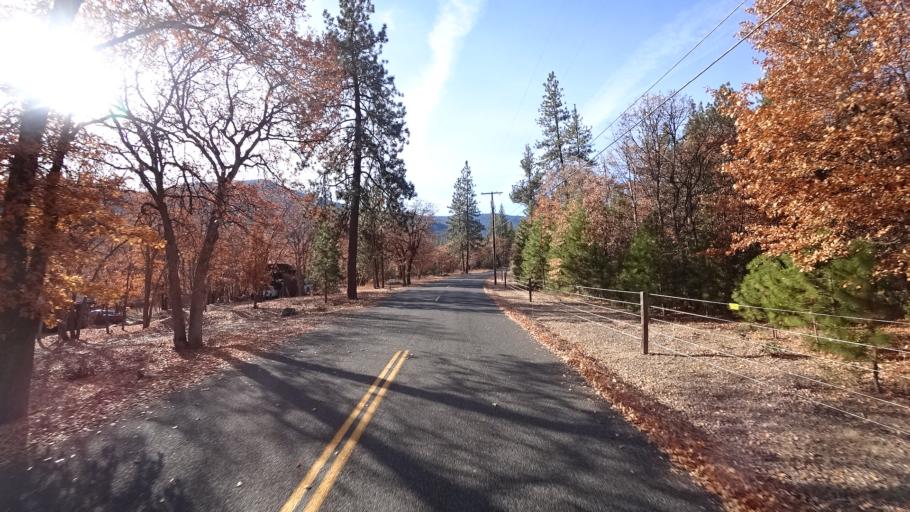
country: US
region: California
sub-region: Siskiyou County
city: Yreka
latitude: 41.6574
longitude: -122.6259
